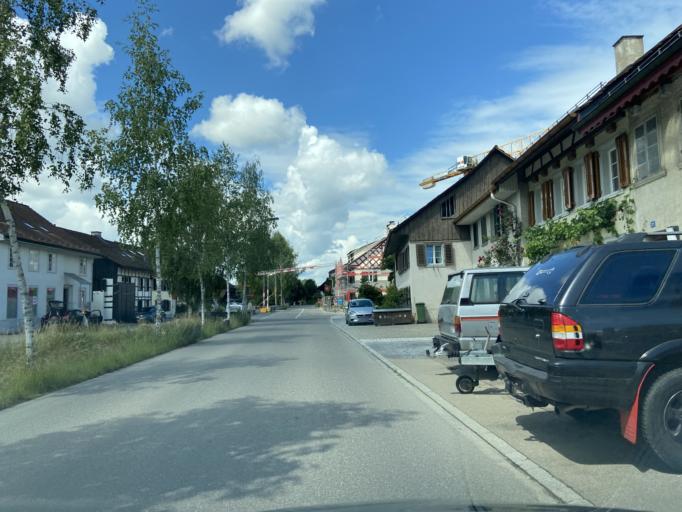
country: CH
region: Zurich
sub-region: Bezirk Winterthur
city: Wiesendangen / Wiesendangen (Dorf)
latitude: 47.5210
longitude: 8.7884
